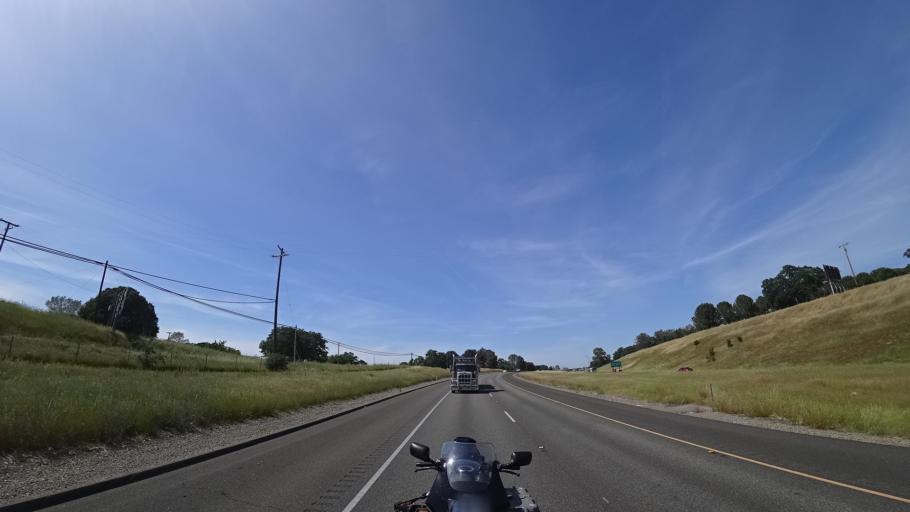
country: US
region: California
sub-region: Shasta County
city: Cottonwood
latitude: 40.2866
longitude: -122.2780
